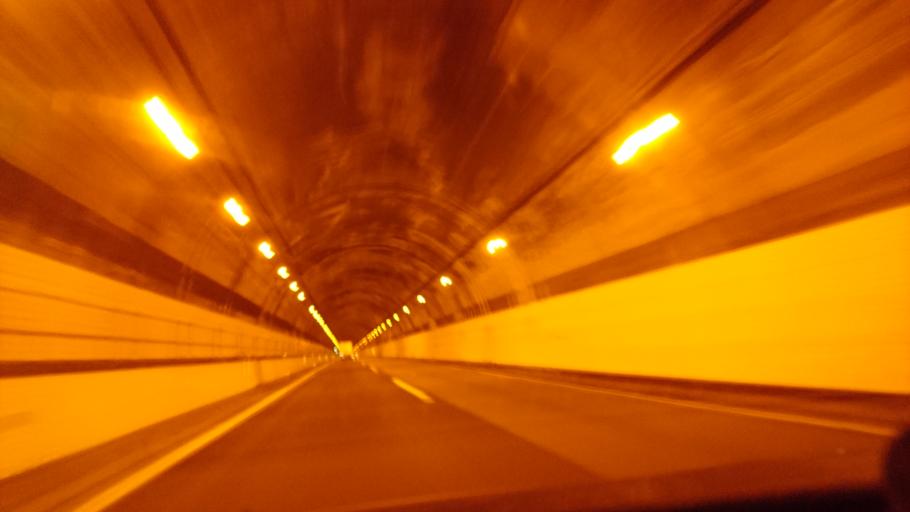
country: JP
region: Iwate
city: Ichinoseki
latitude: 38.9901
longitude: 141.1003
